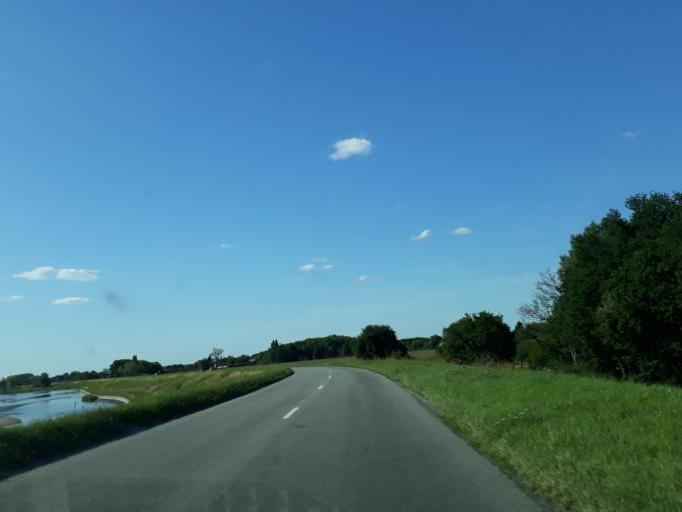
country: FR
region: Centre
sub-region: Departement du Loiret
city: Saint-Benoit-sur-Loire
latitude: 47.8228
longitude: 2.2976
